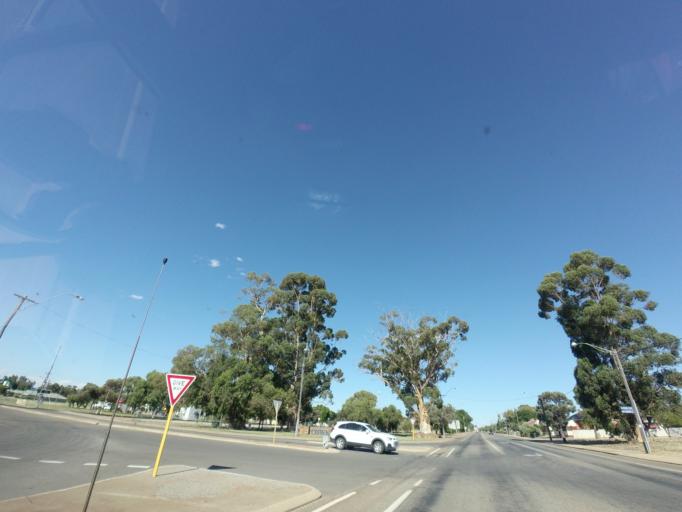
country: AU
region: Western Australia
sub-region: Merredin
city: Merredin
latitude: -31.4829
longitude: 118.2723
